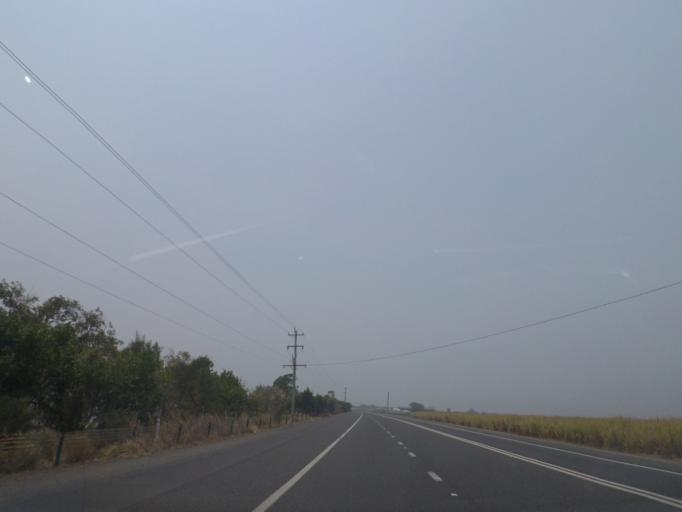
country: AU
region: New South Wales
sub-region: Richmond Valley
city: Evans Head
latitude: -28.9962
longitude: 153.4540
